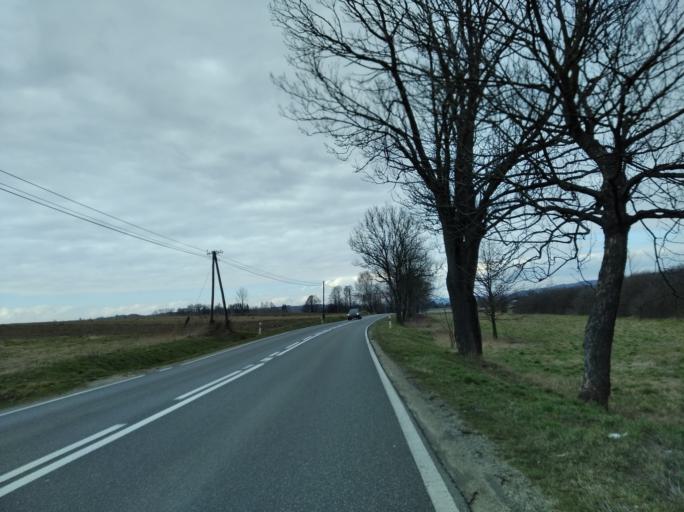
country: PL
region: Subcarpathian Voivodeship
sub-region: Powiat krosnienski
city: Wojaszowka
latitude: 49.7869
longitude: 21.6613
